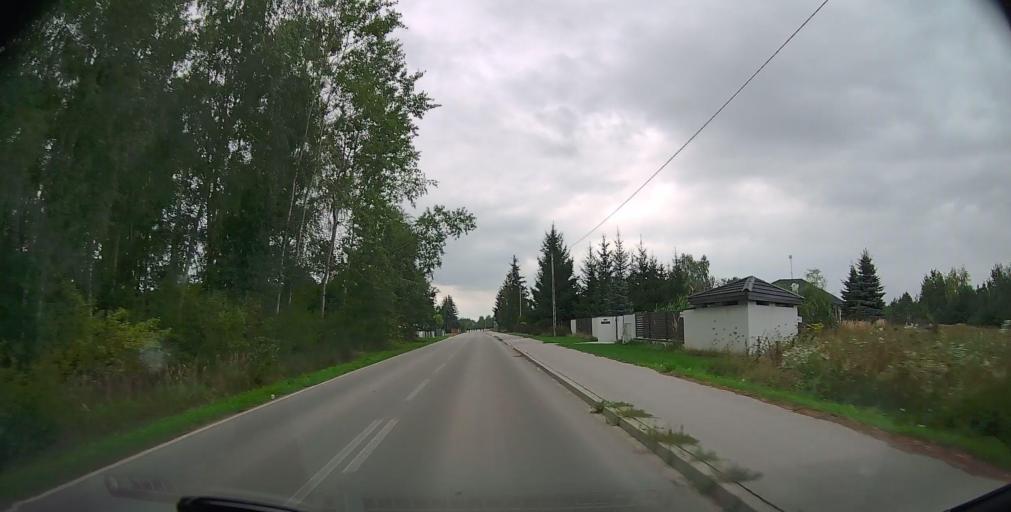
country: PL
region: Masovian Voivodeship
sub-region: Powiat radomski
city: Zakrzew
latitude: 51.4300
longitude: 21.0573
